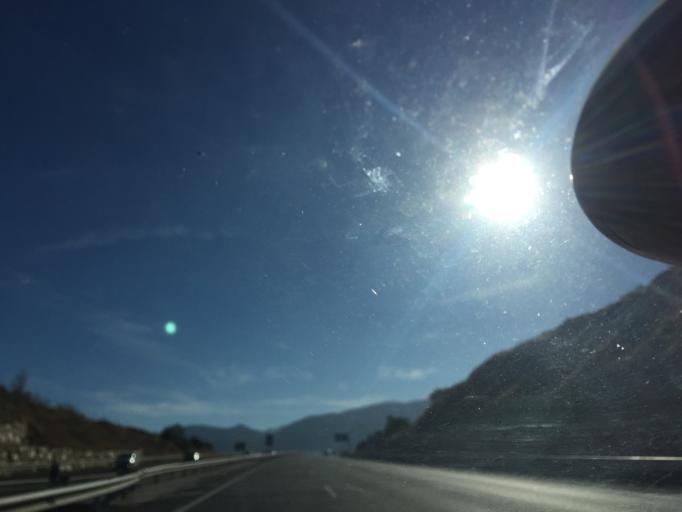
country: ES
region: Andalusia
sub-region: Provincia de Jaen
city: La Guardia de Jaen
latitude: 37.7605
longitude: -3.7122
